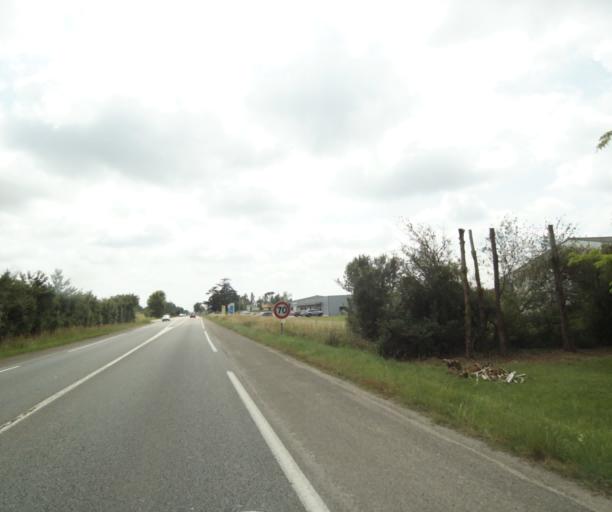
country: FR
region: Midi-Pyrenees
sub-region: Departement du Tarn-et-Garonne
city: Albias
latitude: 44.0551
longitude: 1.4025
